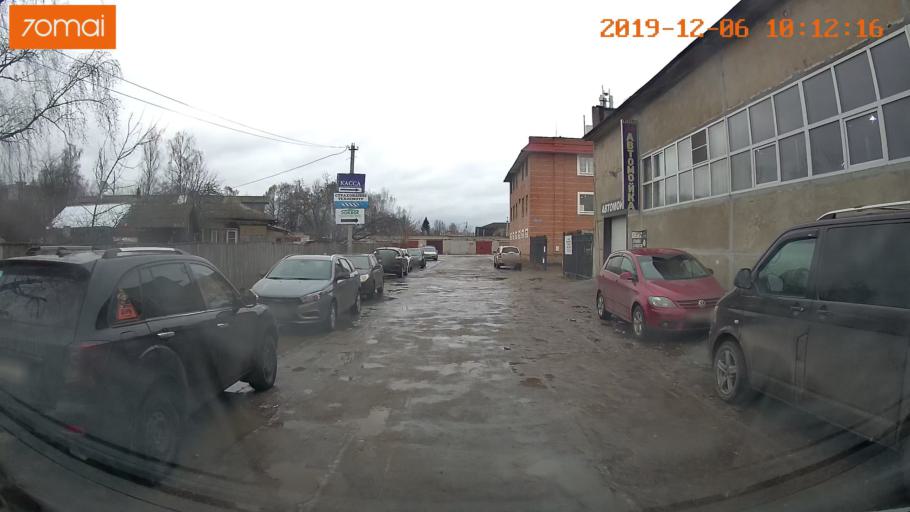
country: RU
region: Ivanovo
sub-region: Gorod Ivanovo
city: Ivanovo
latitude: 57.0323
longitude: 40.9742
